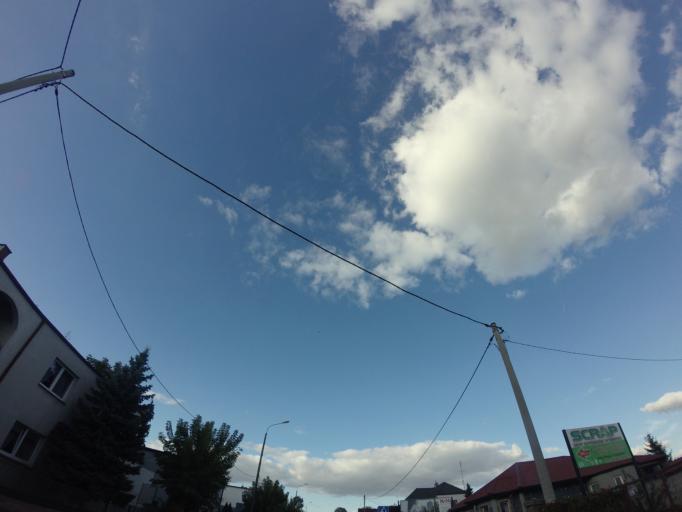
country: PL
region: Greater Poland Voivodeship
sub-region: Powiat nowotomyski
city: Nowy Tomysl
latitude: 52.3021
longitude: 16.1278
